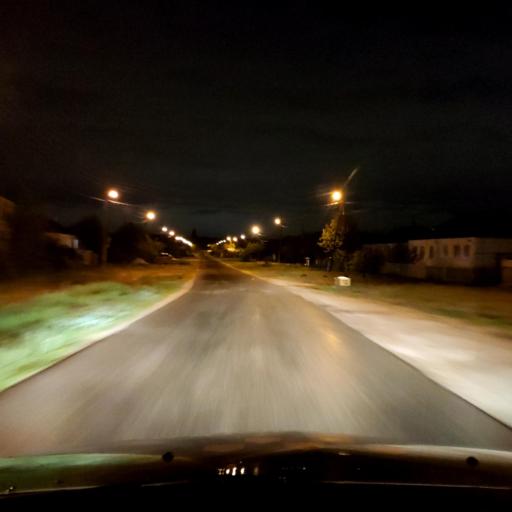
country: RU
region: Voronezj
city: Maslovka
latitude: 51.5808
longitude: 39.3015
